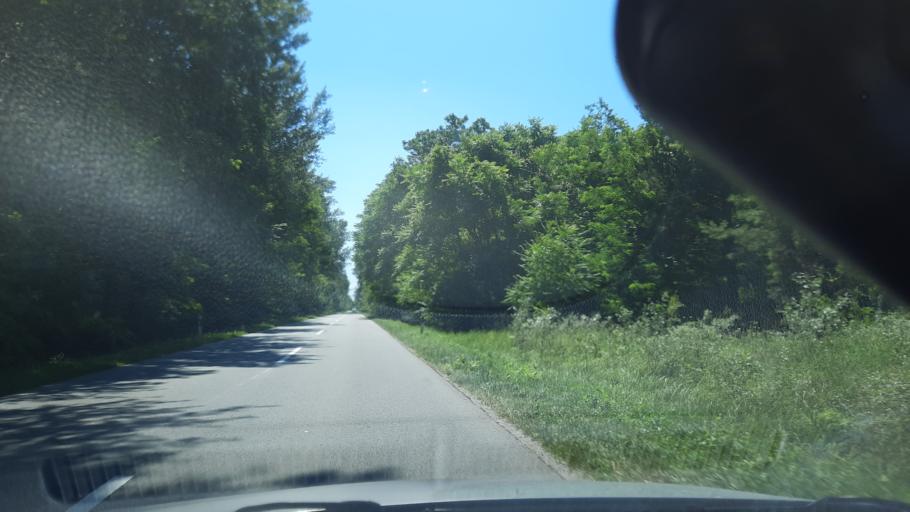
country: RO
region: Caras-Severin
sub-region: Comuna Socol
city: Socol
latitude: 44.8405
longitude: 21.2685
